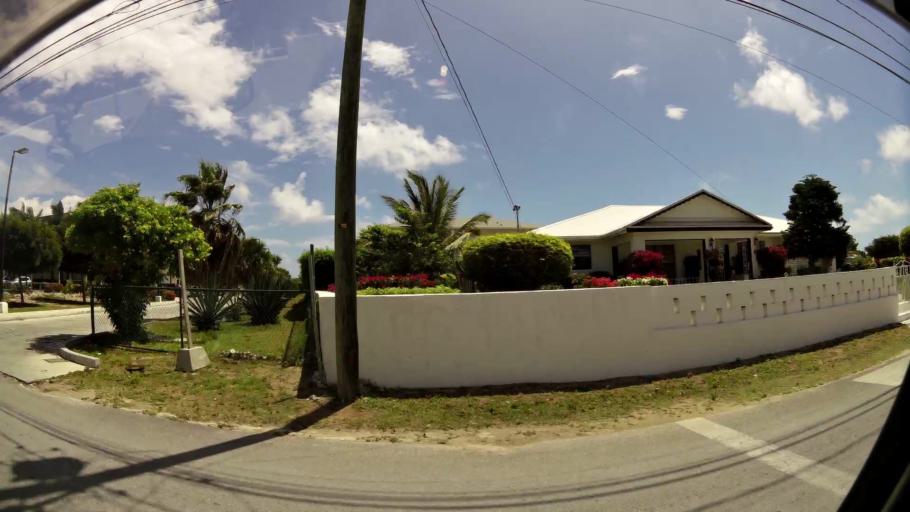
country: TC
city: Cockburn Town
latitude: 21.4795
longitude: -71.1447
